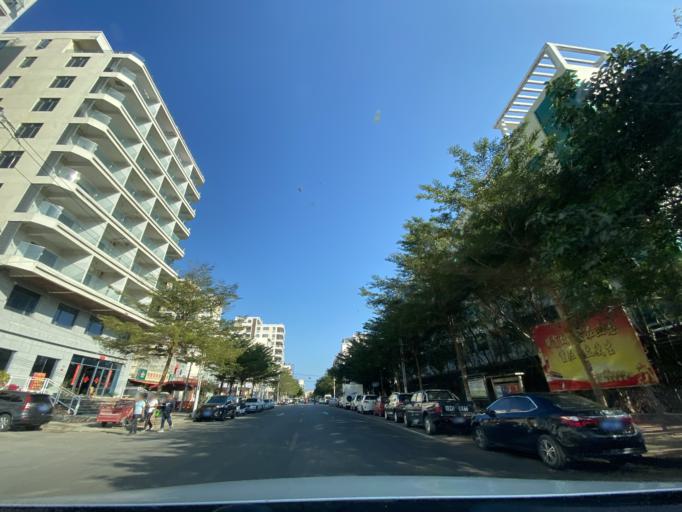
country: CN
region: Hainan
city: Xincun
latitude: 18.4149
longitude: 109.9613
